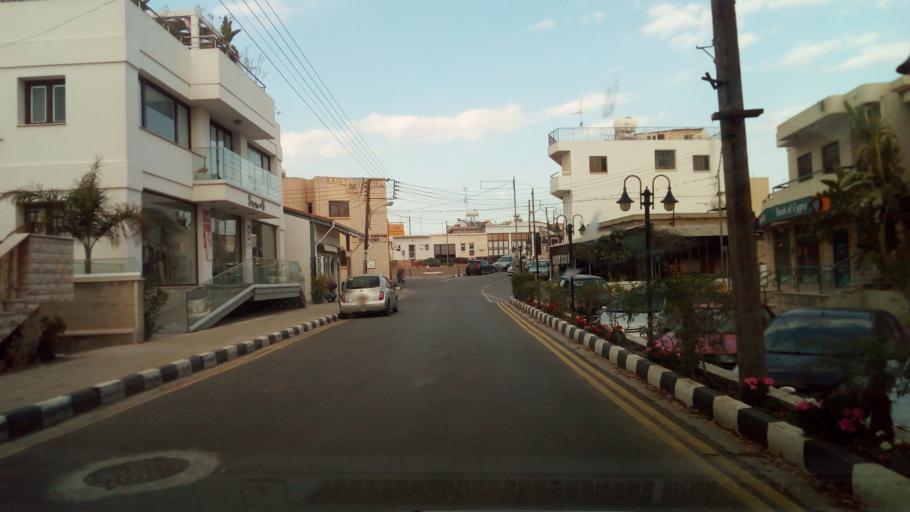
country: CY
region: Larnaka
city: Xylotymbou
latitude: 35.0170
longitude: 33.7430
